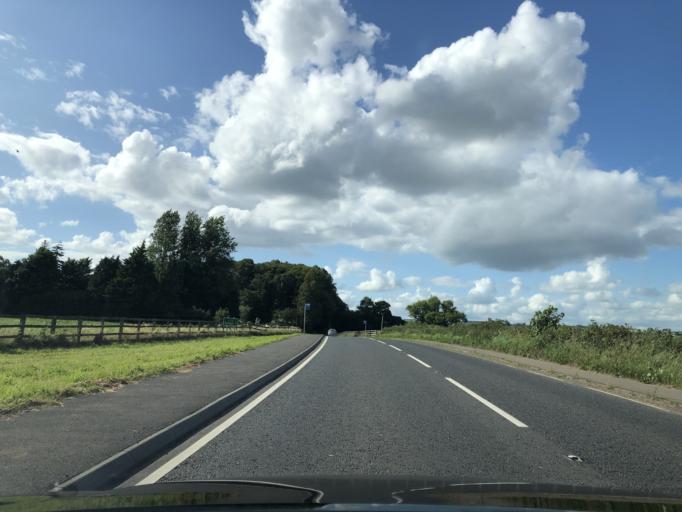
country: GB
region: Northern Ireland
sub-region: Ards District
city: Comber
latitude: 54.5617
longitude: -5.7634
